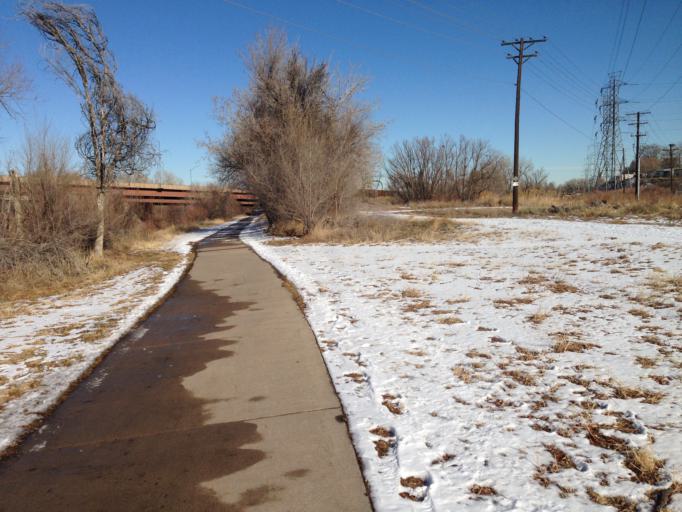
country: US
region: Colorado
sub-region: Adams County
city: Berkley
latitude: 39.7983
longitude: -105.0329
